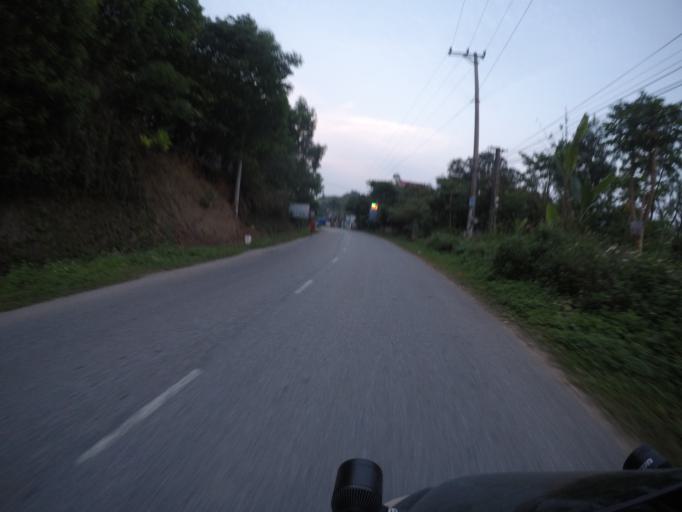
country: VN
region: Thai Nguyen
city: Chua Hang
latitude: 21.5851
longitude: 105.7013
